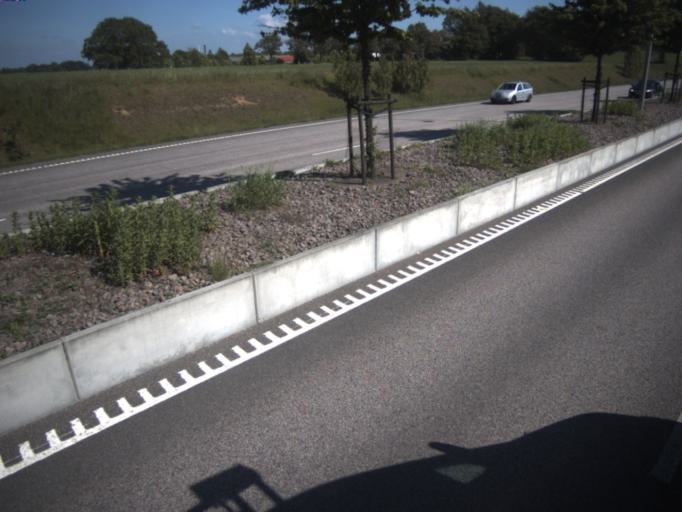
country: SE
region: Skane
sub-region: Helsingborg
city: Odakra
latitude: 56.0434
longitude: 12.7567
